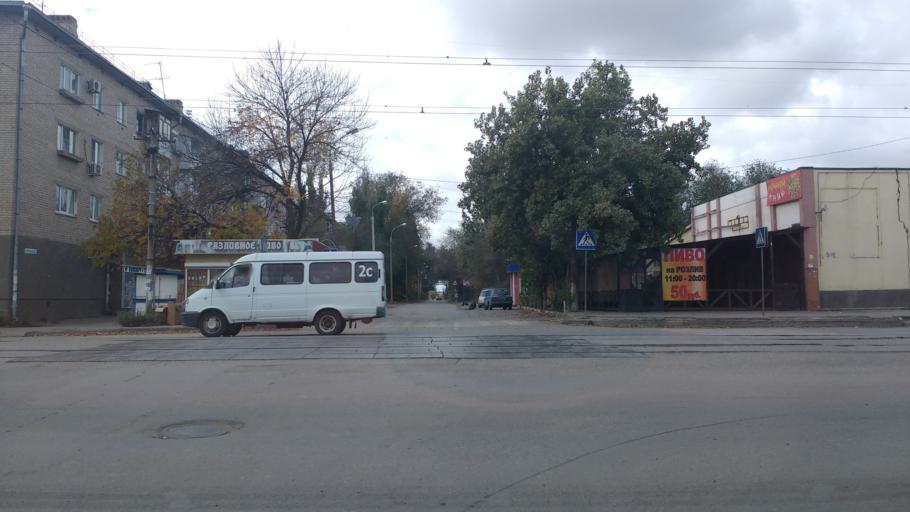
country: RU
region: Volgograd
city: Vodstroy
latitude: 48.7746
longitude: 44.5450
